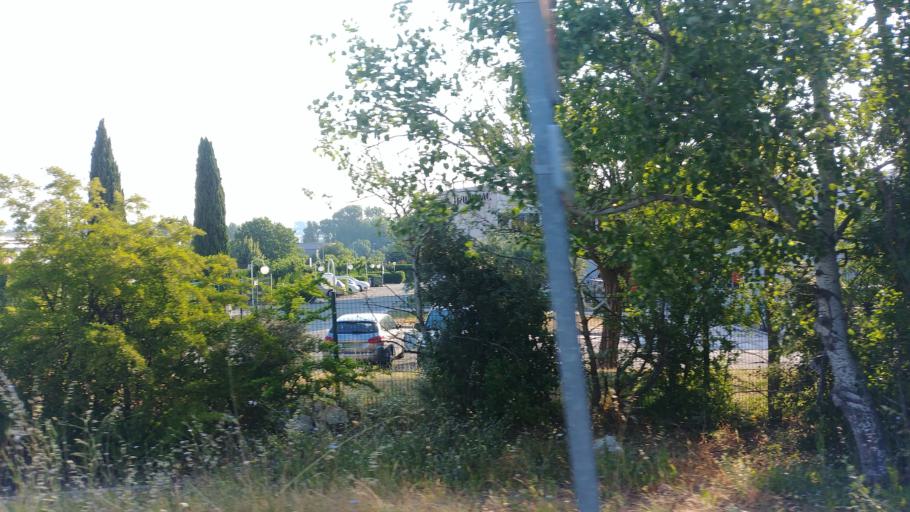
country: FR
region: Provence-Alpes-Cote d'Azur
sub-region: Departement des Bouches-du-Rhone
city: Cabries
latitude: 43.4788
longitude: 5.3715
